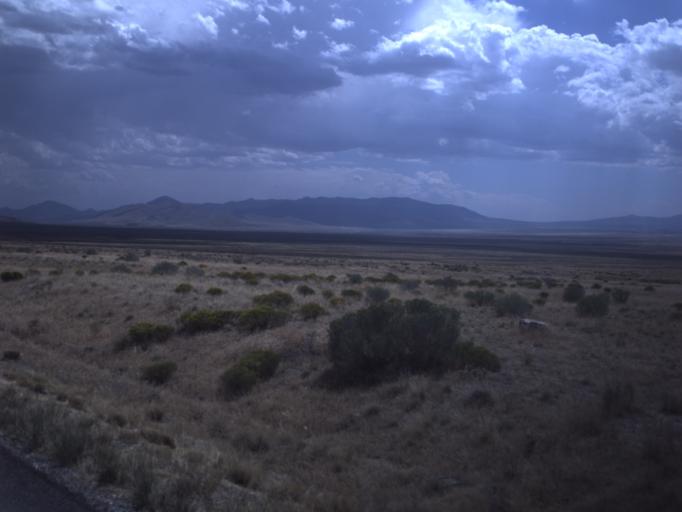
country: US
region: Utah
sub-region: Utah County
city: Eagle Mountain
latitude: 40.2599
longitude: -112.2304
